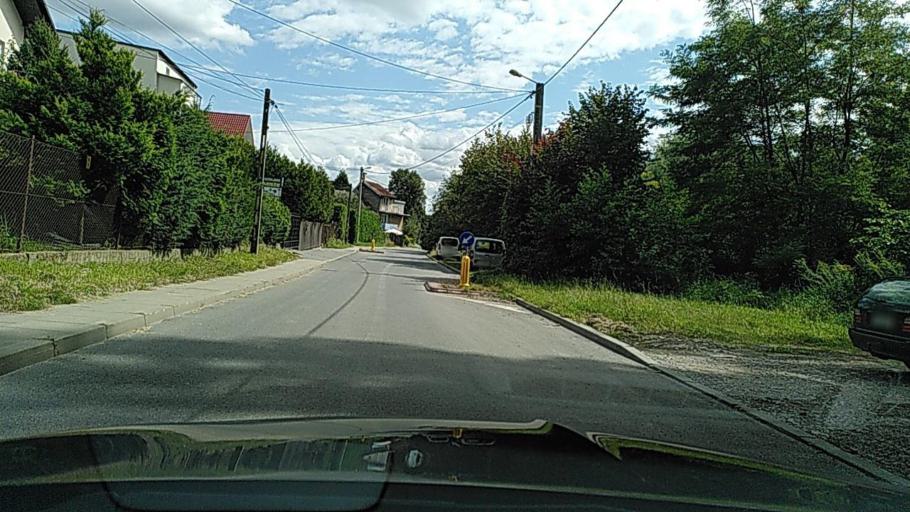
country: PL
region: Lesser Poland Voivodeship
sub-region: Powiat krakowski
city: Rzaska
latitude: 50.0895
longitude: 19.8719
